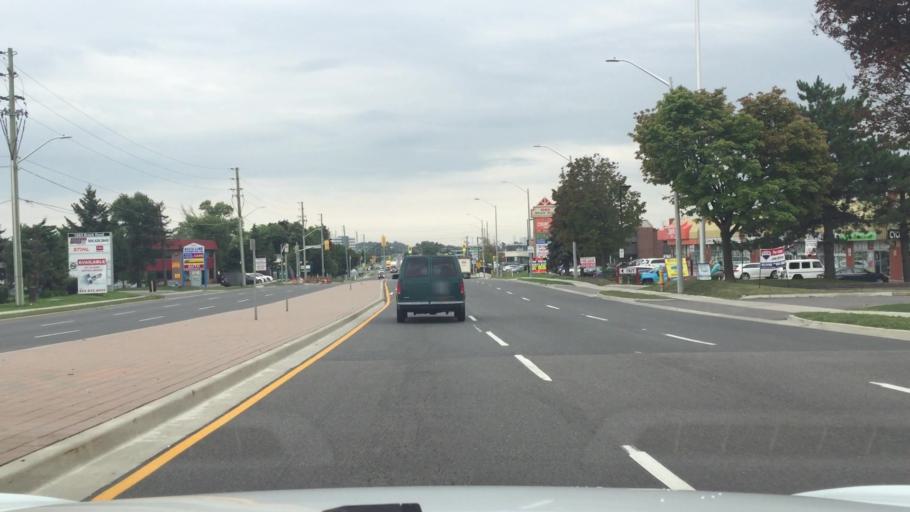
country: CA
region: Ontario
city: Ajax
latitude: 43.8362
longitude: -79.0692
